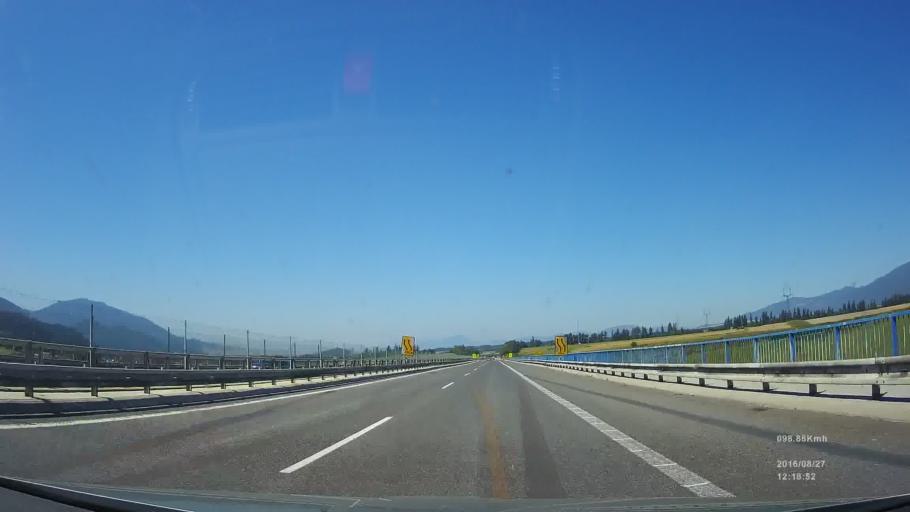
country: SK
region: Zilinsky
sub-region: Okres Liptovsky Mikulas
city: Pribylina
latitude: 49.0525
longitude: 19.7770
